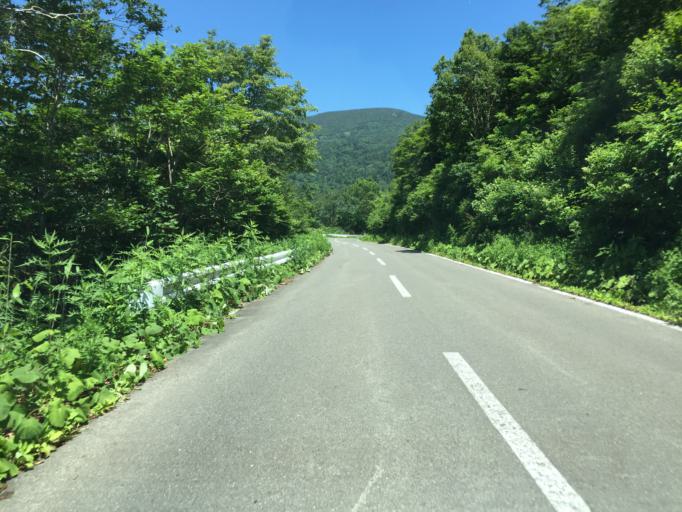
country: JP
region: Fukushima
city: Inawashiro
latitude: 37.6809
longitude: 140.2312
